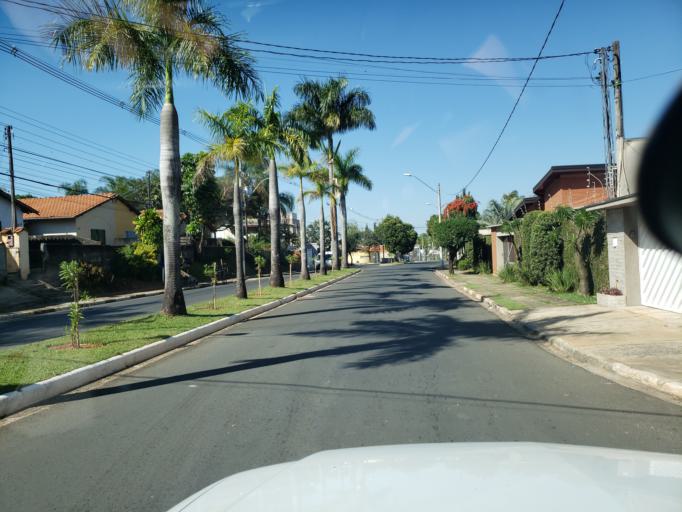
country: BR
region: Sao Paulo
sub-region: Itapira
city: Itapira
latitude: -22.4250
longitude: -46.8371
